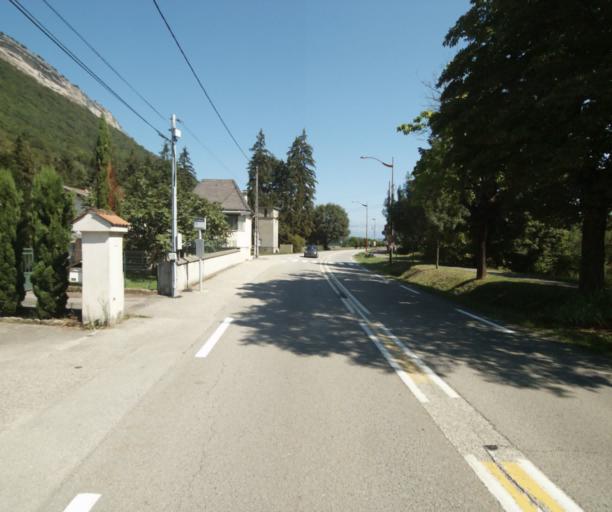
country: FR
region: Rhone-Alpes
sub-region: Departement de l'Isere
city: Vif
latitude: 45.0630
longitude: 5.6693
